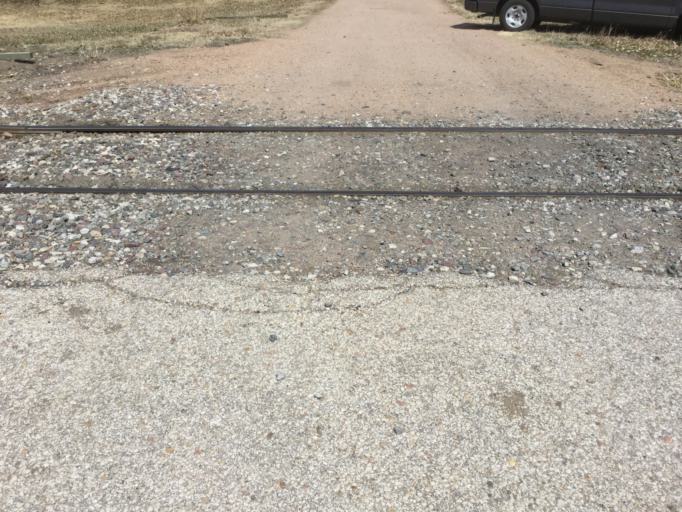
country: US
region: Kansas
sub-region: Barton County
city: Great Bend
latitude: 38.4220
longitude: -98.8902
